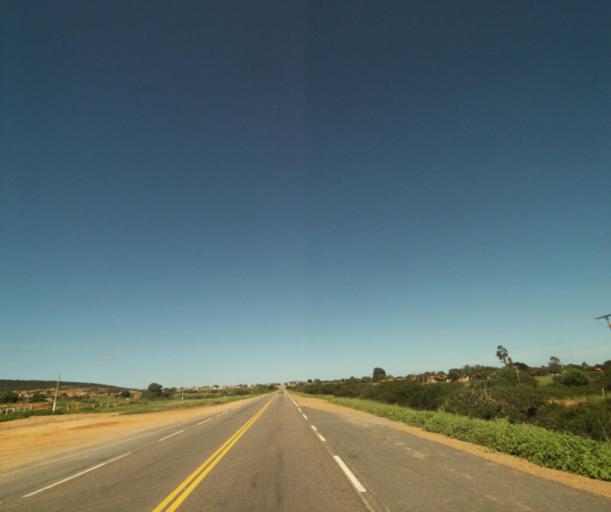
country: BR
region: Bahia
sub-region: Palmas De Monte Alto
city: Palmas de Monte Alto
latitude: -14.2491
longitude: -43.1576
